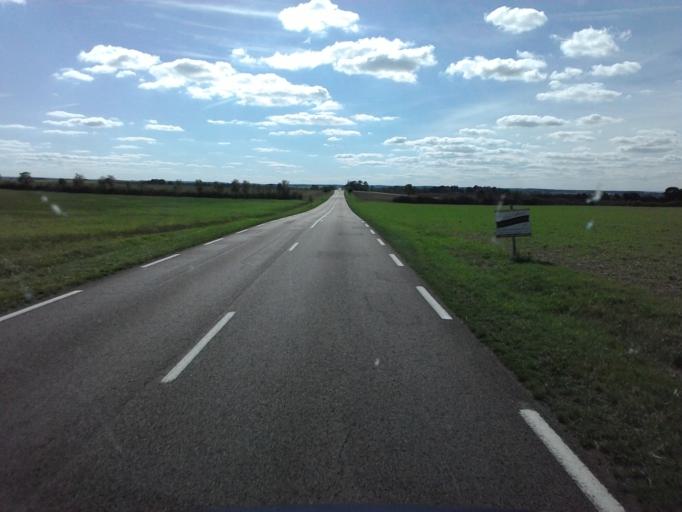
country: FR
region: Bourgogne
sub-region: Departement de la Cote-d'Or
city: Chatillon-sur-Seine
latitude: 47.8909
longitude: 4.6047
